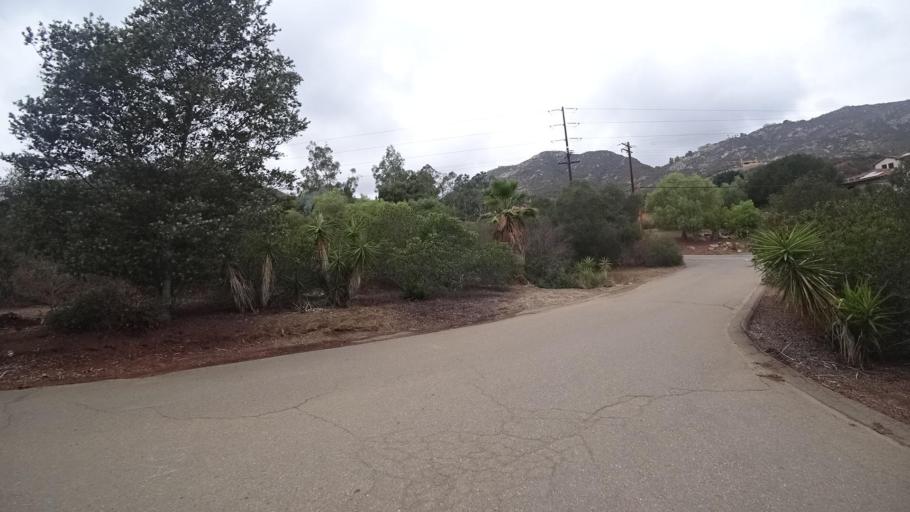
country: US
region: California
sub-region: San Diego County
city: Escondido
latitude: 33.0616
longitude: -117.1221
